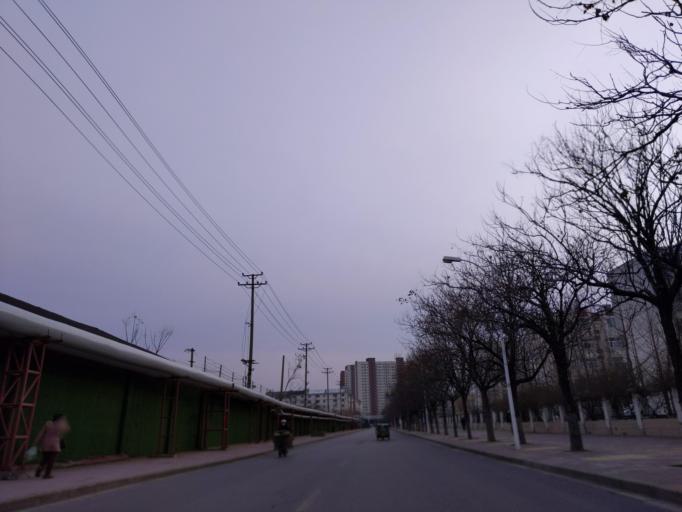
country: CN
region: Henan Sheng
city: Puyang
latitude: 35.7554
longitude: 115.0393
